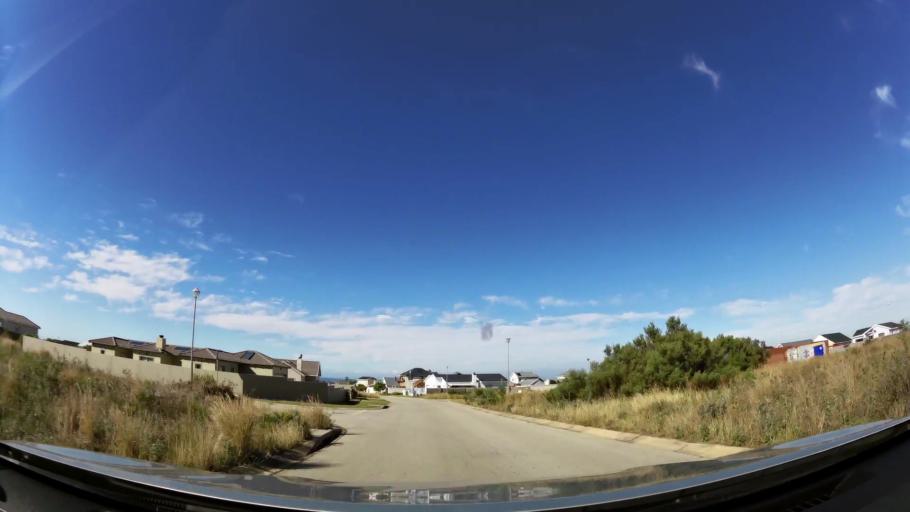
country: ZA
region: Eastern Cape
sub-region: Cacadu District Municipality
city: Jeffrey's Bay
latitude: -34.0337
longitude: 24.9030
